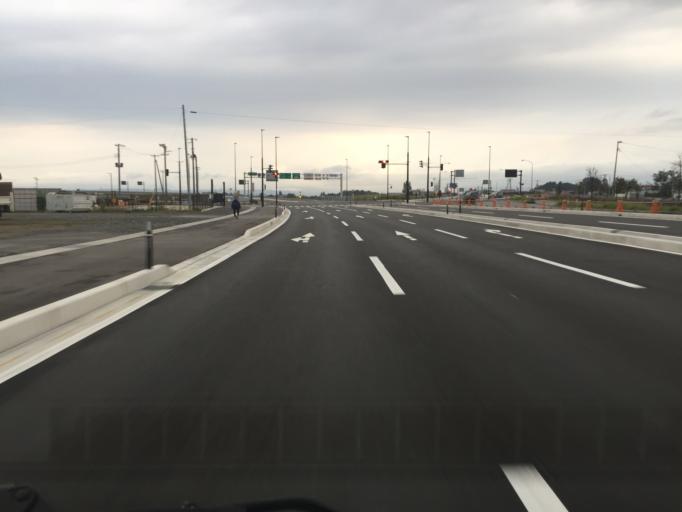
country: JP
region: Fukushima
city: Kitakata
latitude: 37.5341
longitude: 139.9151
